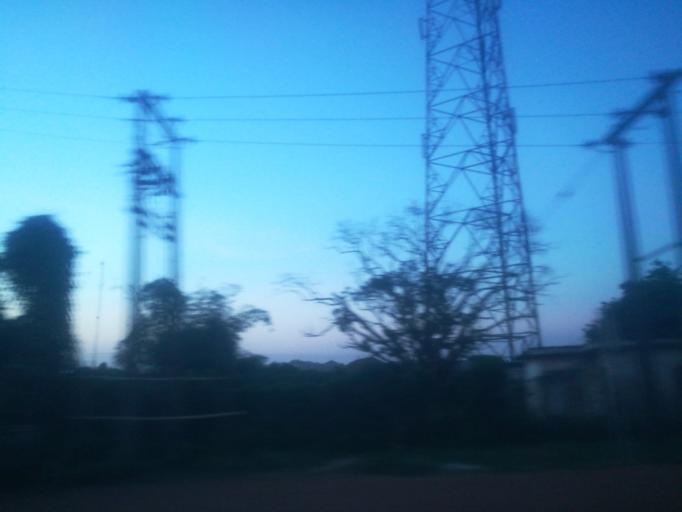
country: NG
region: Ogun
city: Abeokuta
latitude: 7.1883
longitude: 3.4370
